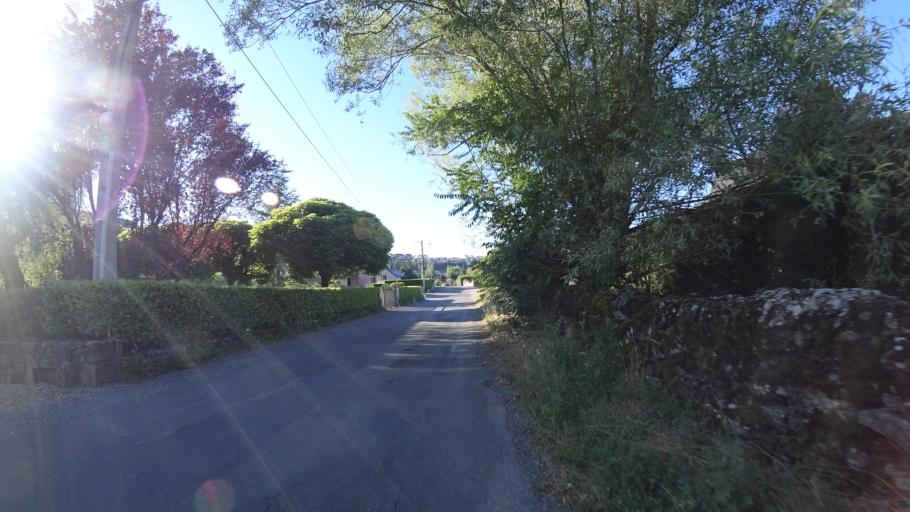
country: FR
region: Midi-Pyrenees
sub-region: Departement de l'Aveyron
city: Rodez
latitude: 44.3697
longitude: 2.5741
